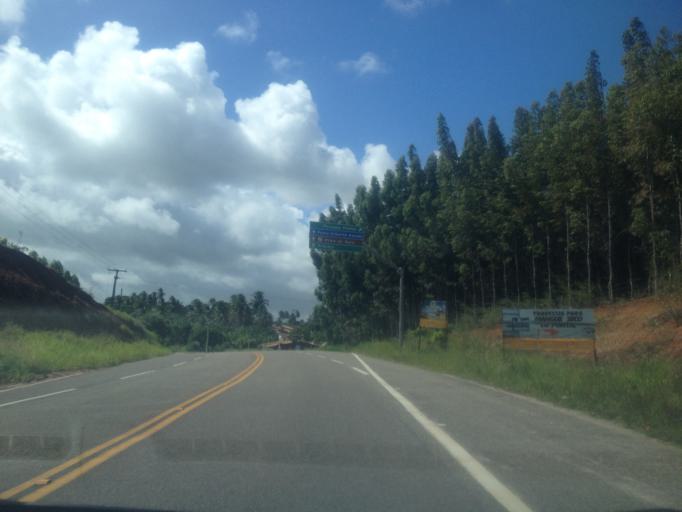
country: BR
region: Sergipe
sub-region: Indiaroba
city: Indiaroba
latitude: -11.4851
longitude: -37.4699
